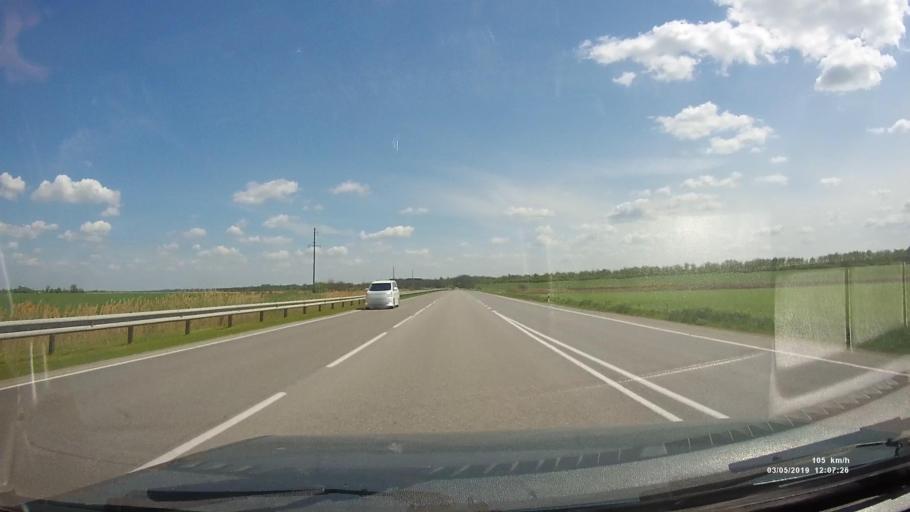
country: RU
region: Rostov
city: Bagayevskaya
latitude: 47.2848
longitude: 40.4749
